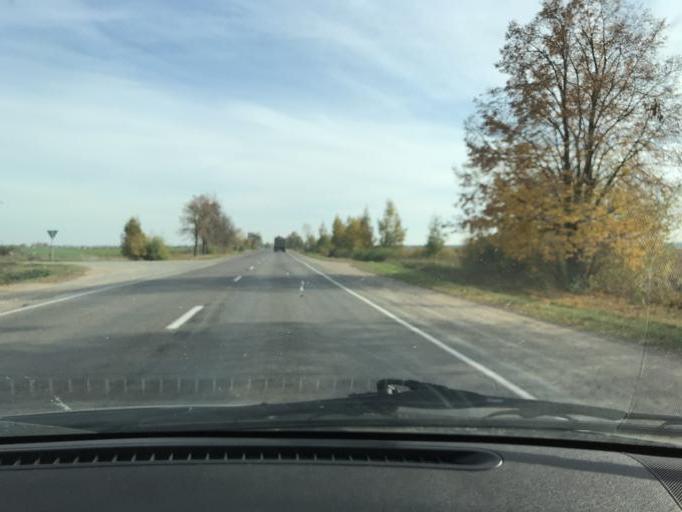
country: BY
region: Brest
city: Asnyezhytsy
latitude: 52.2134
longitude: 26.0436
